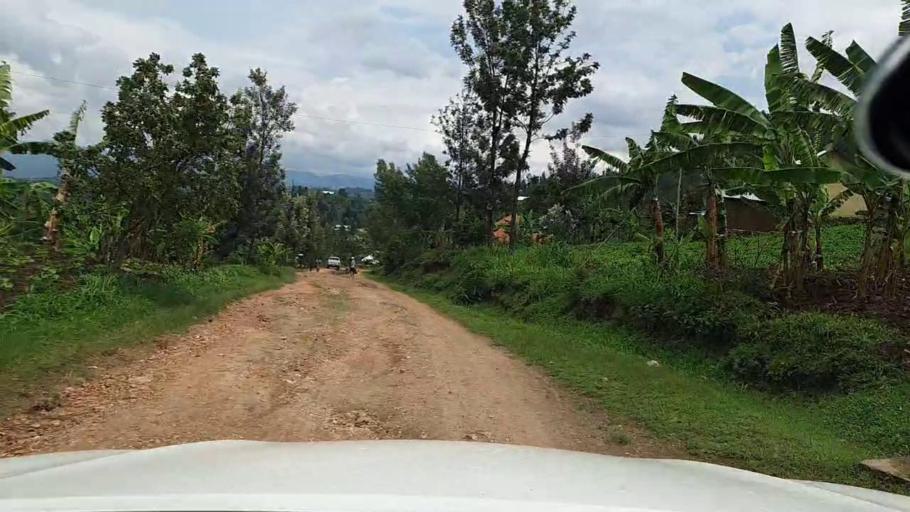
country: RW
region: Western Province
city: Kibuye
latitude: -2.0818
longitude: 29.4206
